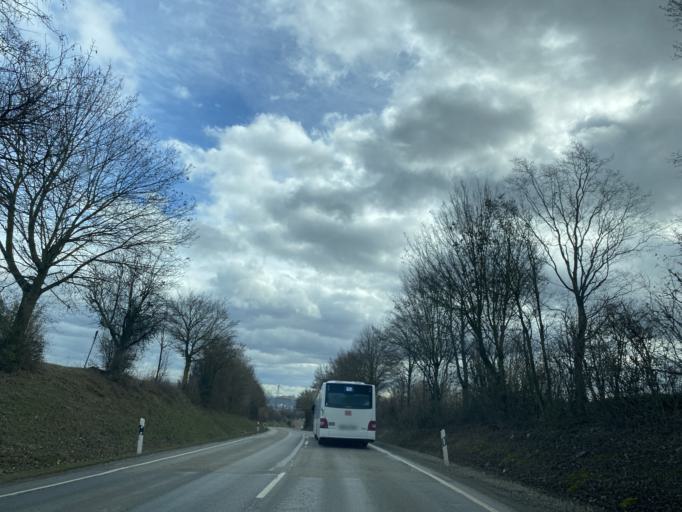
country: DE
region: Baden-Wuerttemberg
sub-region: Regierungsbezirk Stuttgart
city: Hemmingen
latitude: 48.8388
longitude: 9.0241
